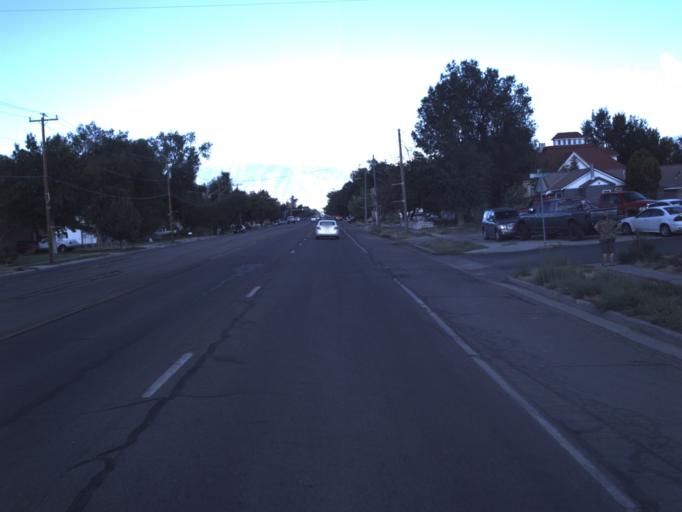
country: US
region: Utah
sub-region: Tooele County
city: Grantsville
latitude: 40.5998
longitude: -112.4627
